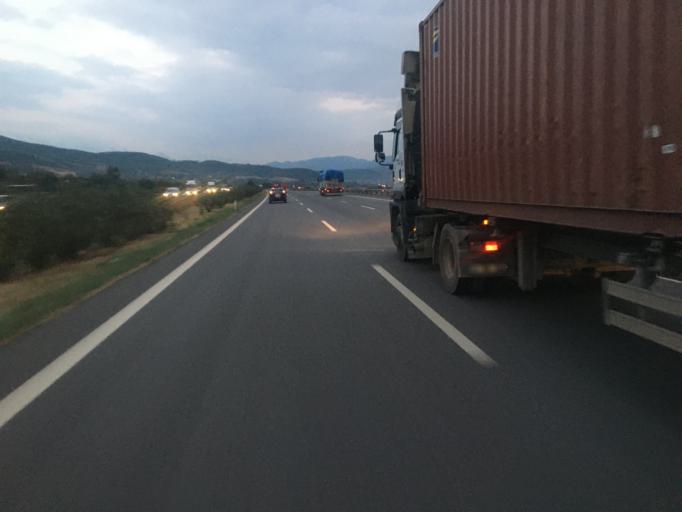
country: TR
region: Osmaniye
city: Osmaniye
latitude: 37.1353
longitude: 36.3120
